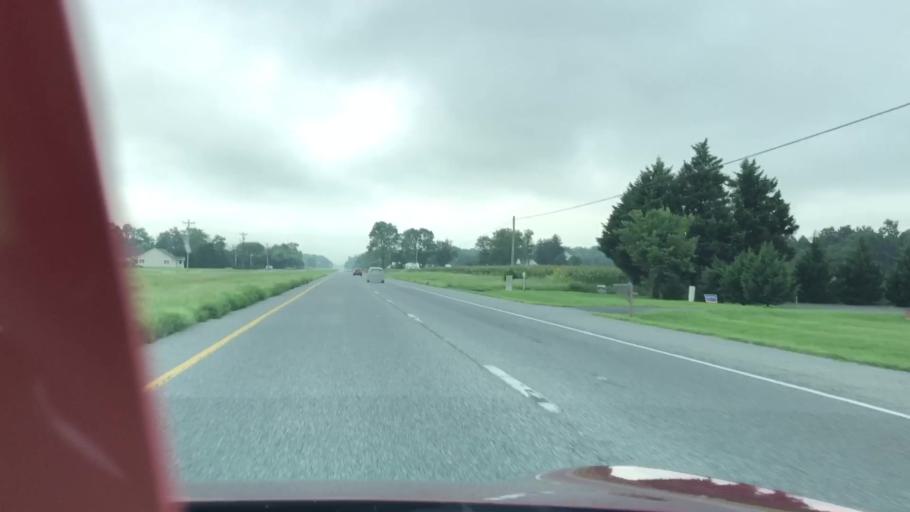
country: US
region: Delaware
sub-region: Sussex County
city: Bridgeville
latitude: 38.7854
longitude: -75.5917
